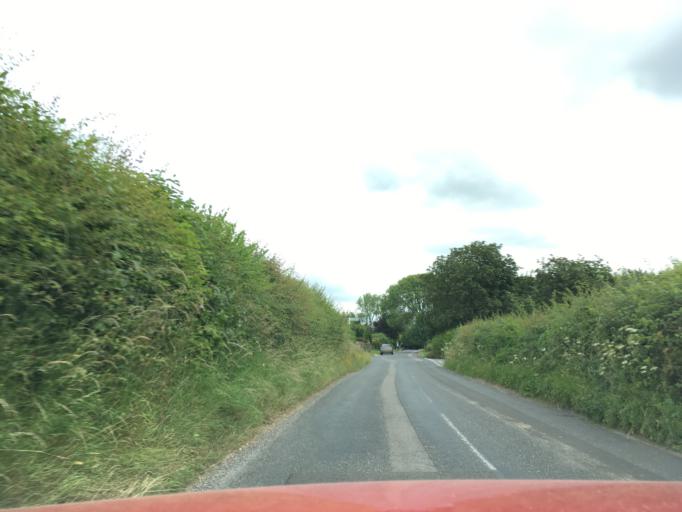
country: GB
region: England
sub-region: Oxfordshire
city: Shipton under Wychwood
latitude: 51.8768
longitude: -1.6635
